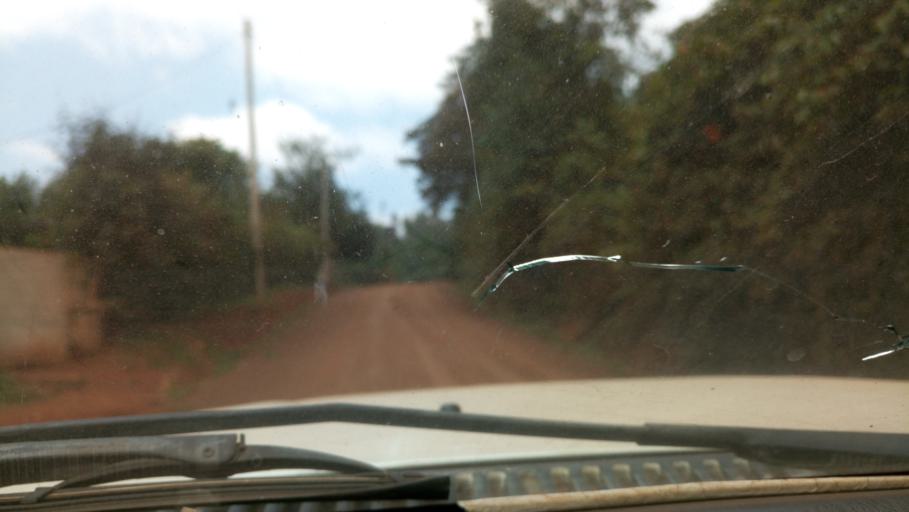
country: KE
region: Murang'a District
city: Maragua
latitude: -0.8170
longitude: 37.0024
